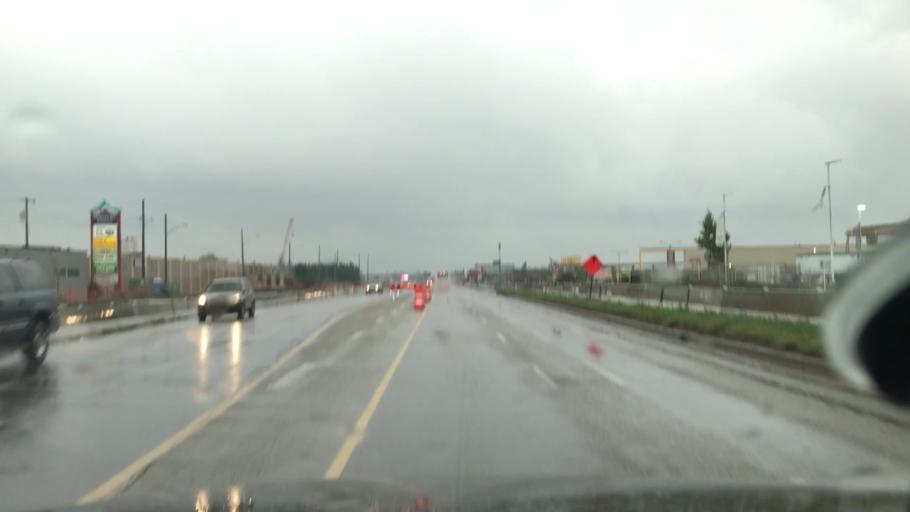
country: CA
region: Alberta
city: Edmonton
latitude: 53.4939
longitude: -113.4427
